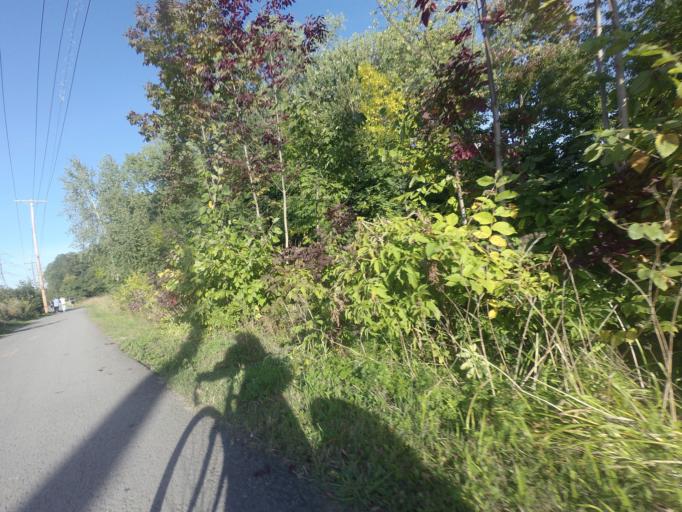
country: CA
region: Quebec
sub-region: Laurentides
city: Saint-Jerome
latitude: 45.7790
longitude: -73.9986
